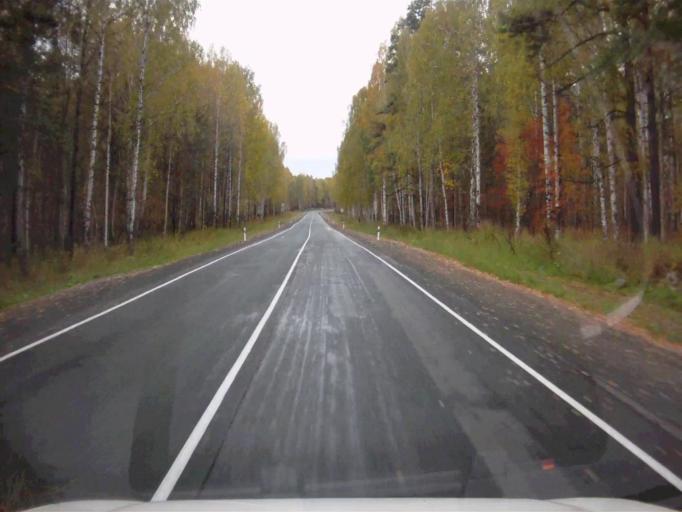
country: RU
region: Chelyabinsk
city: Nyazepetrovsk
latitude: 56.0631
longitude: 59.7254
